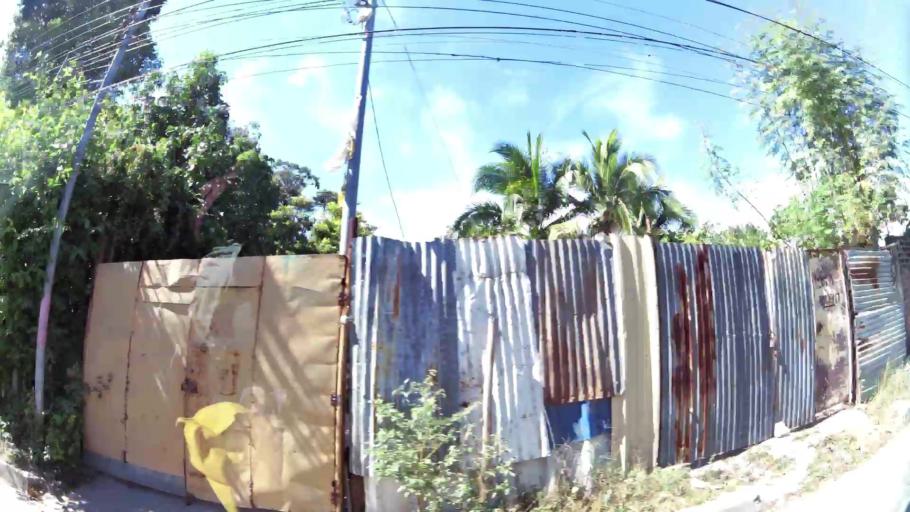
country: SV
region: San Salvador
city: Apopa
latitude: 13.8077
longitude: -89.1735
